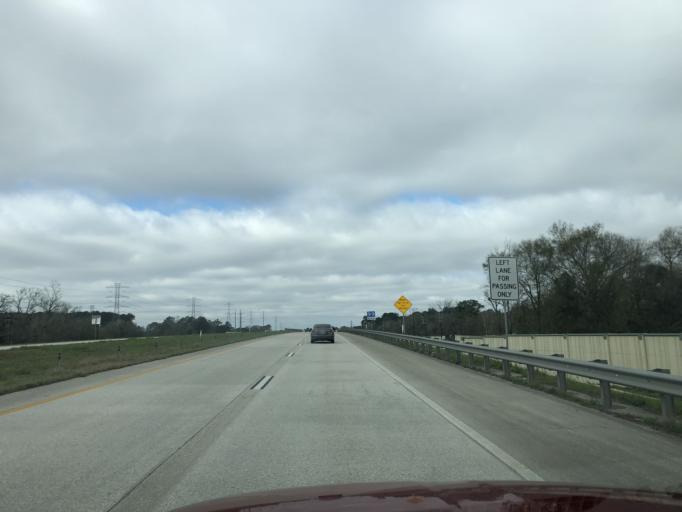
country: US
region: Texas
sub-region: Harris County
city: Spring
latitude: 30.0925
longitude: -95.4757
